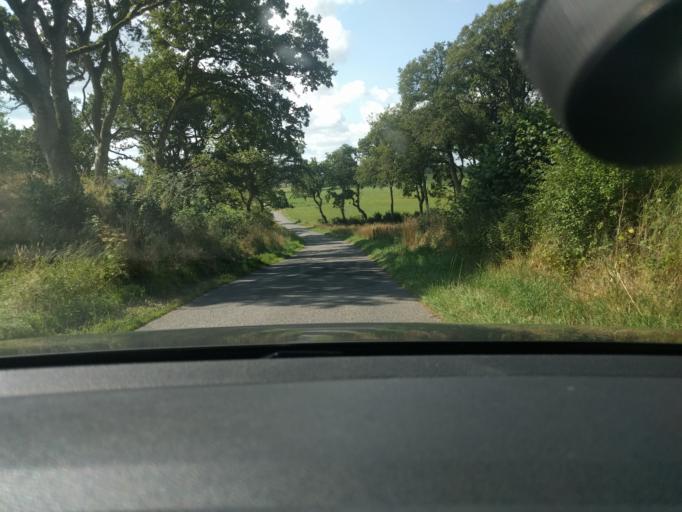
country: DK
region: Central Jutland
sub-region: Viborg Kommune
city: Bjerringbro
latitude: 56.4599
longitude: 9.5914
